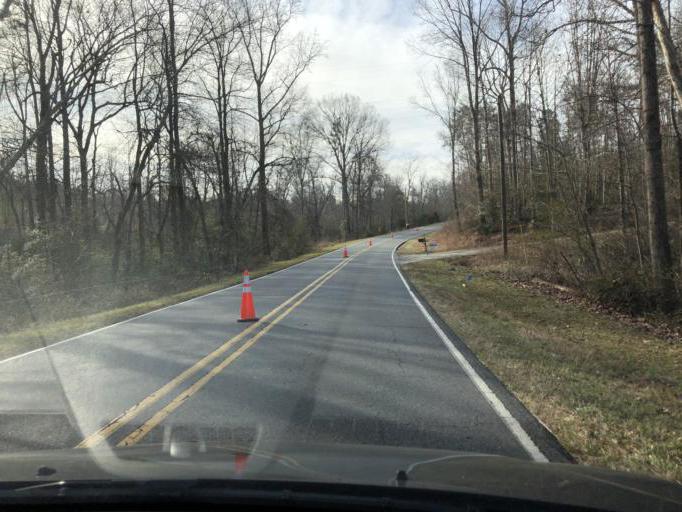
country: US
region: North Carolina
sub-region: Cleveland County
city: Boiling Springs
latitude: 35.2432
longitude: -81.6469
